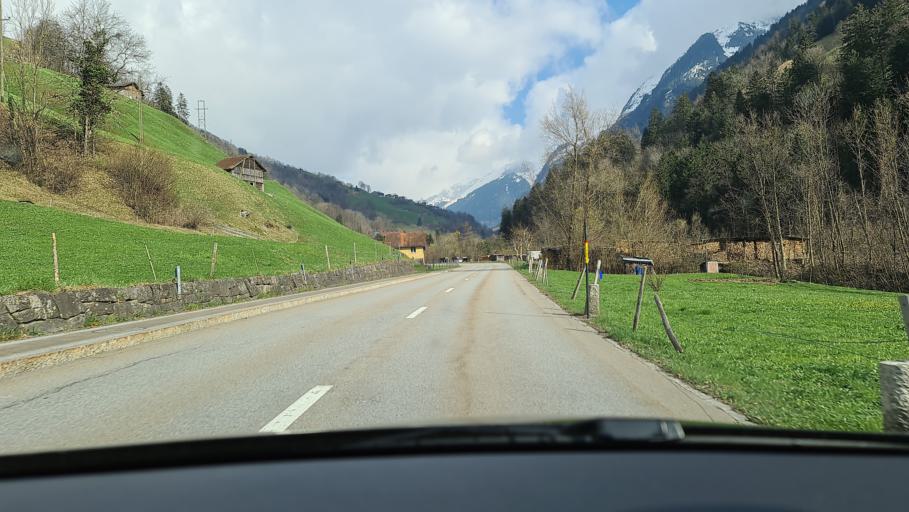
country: CH
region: Uri
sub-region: Uri
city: Burglen
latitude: 46.8791
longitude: 8.7005
